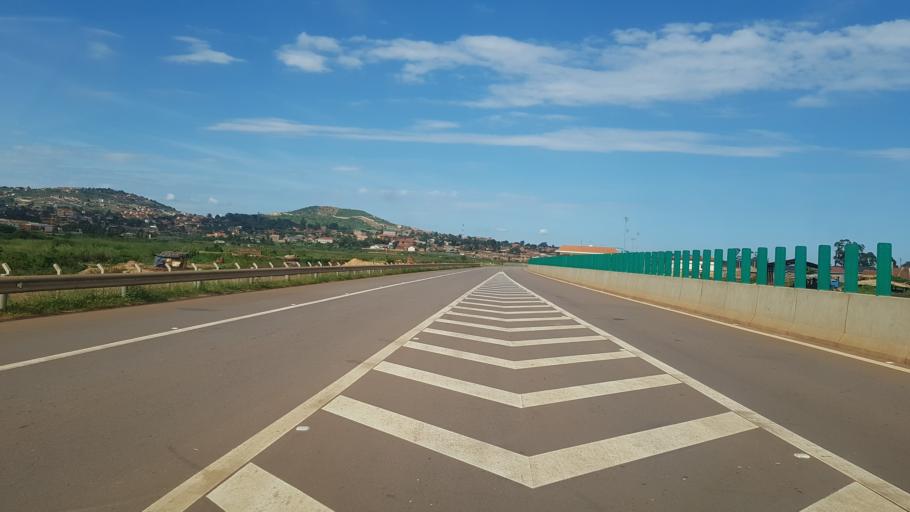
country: UG
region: Central Region
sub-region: Wakiso District
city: Kajansi
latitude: 0.2154
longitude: 32.5337
